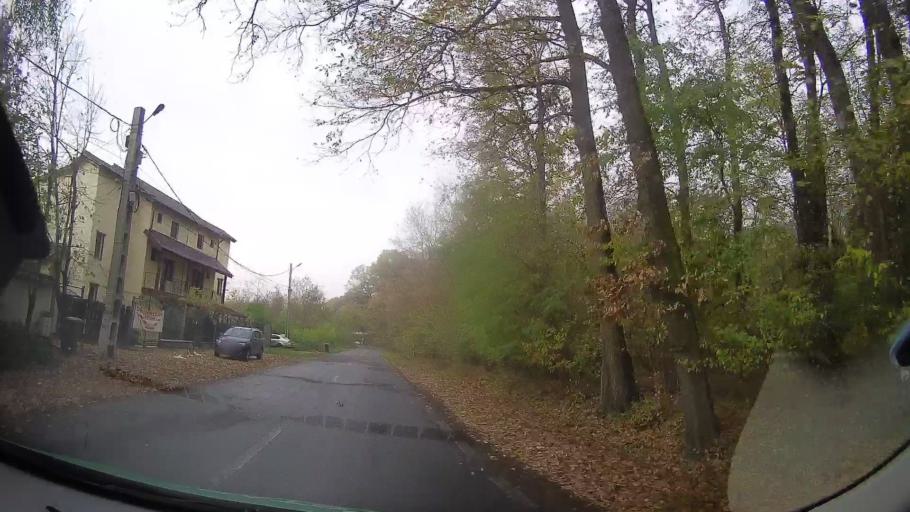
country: RO
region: Ilfov
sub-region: Comuna Snagov
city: Snagov
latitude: 44.7166
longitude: 26.1905
